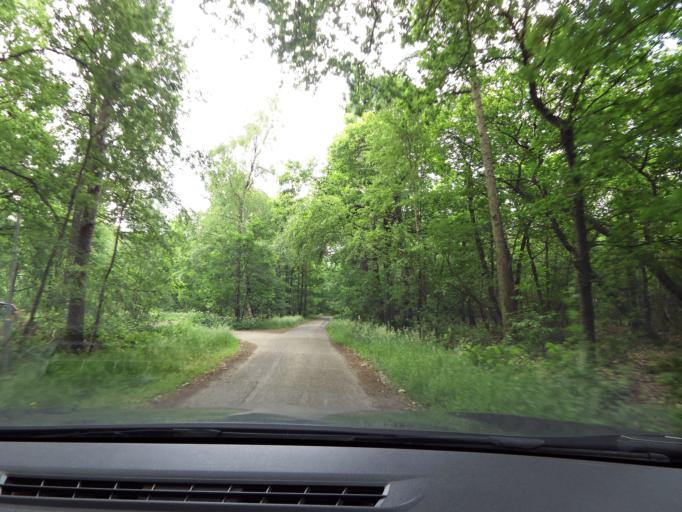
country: NL
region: North Brabant
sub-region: Gemeente Baarle-Nassau
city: Baarle-Nassau
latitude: 51.4974
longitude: 4.9020
